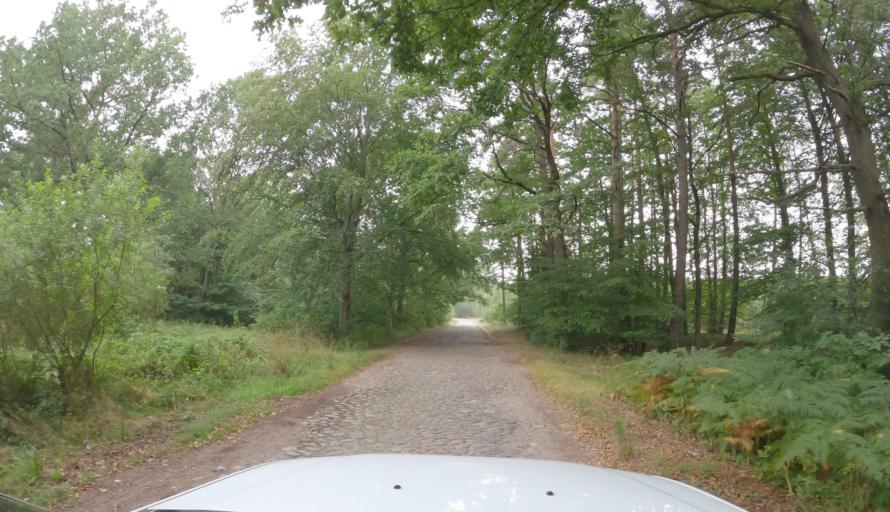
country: PL
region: West Pomeranian Voivodeship
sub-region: Powiat kolobrzeski
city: Ryman
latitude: 53.8566
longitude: 15.5805
